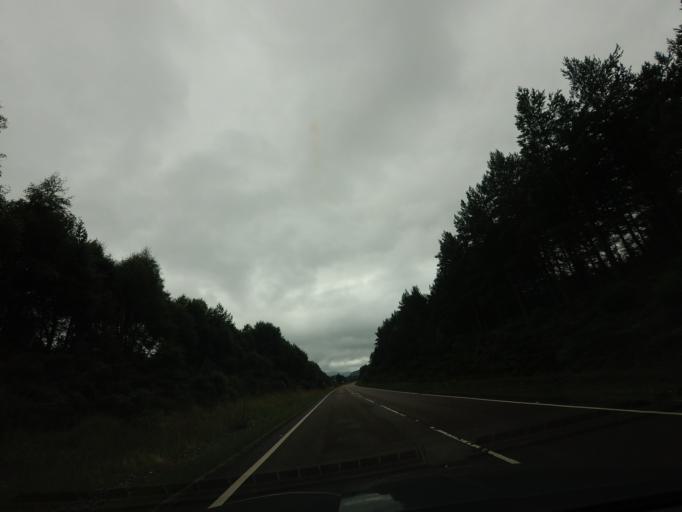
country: GB
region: Scotland
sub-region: Highland
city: Aviemore
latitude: 57.2211
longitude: -3.8207
